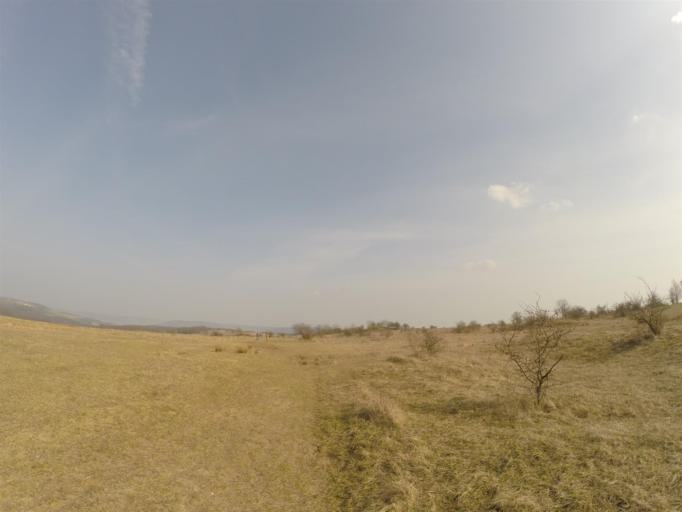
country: DE
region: Thuringia
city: Jena
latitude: 50.9512
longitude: 11.5682
